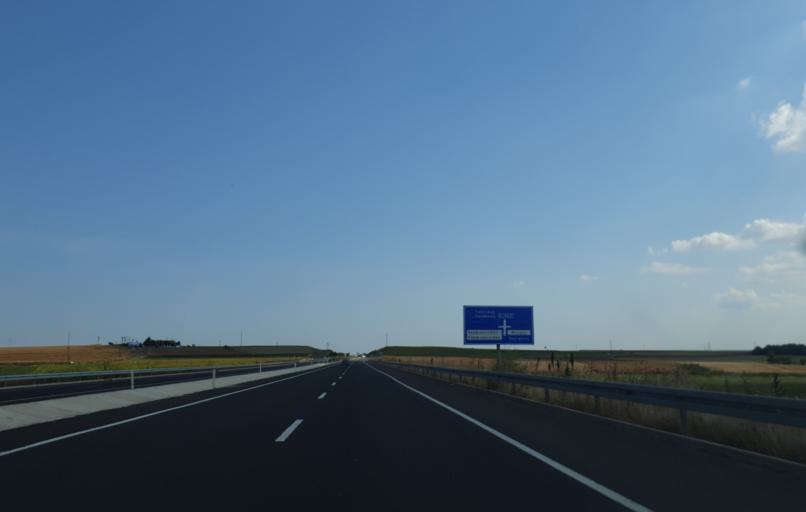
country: TR
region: Tekirdag
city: Muratli
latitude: 41.2158
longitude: 27.5331
